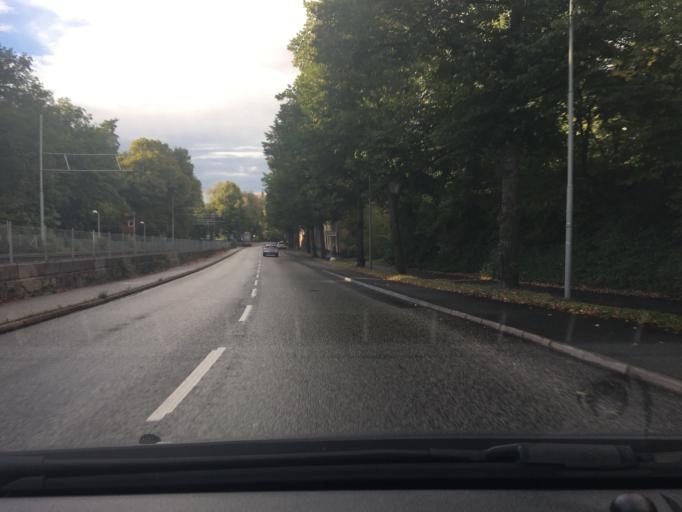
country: SE
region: Stockholm
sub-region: Sundbybergs Kommun
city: Sundbyberg
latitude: 59.3299
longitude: 17.9753
